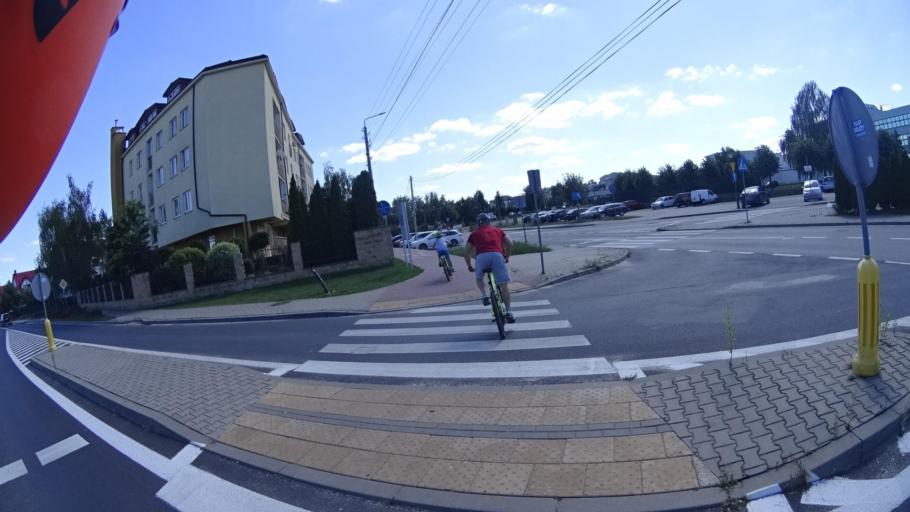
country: PL
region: Masovian Voivodeship
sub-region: Powiat piaseczynski
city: Jozefoslaw
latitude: 52.0987
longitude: 21.0534
